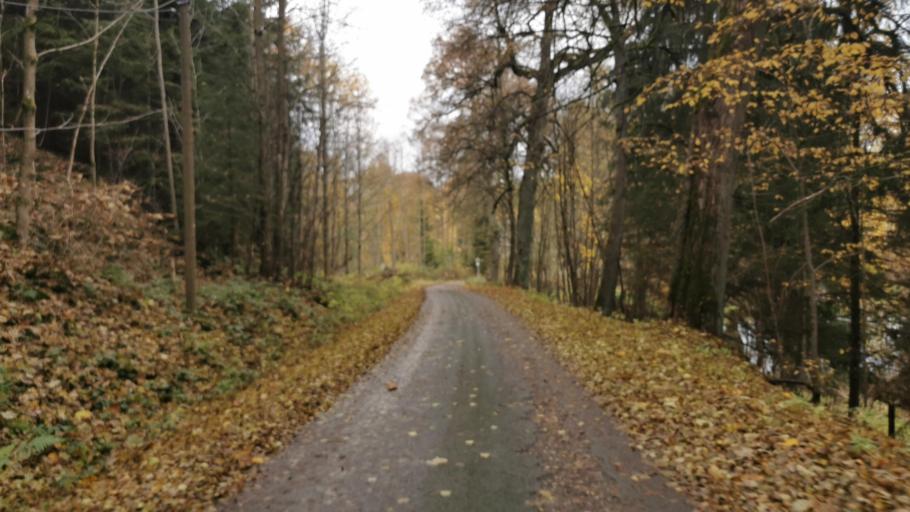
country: DE
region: Thuringia
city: Wurzbach
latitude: 50.4493
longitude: 11.5468
